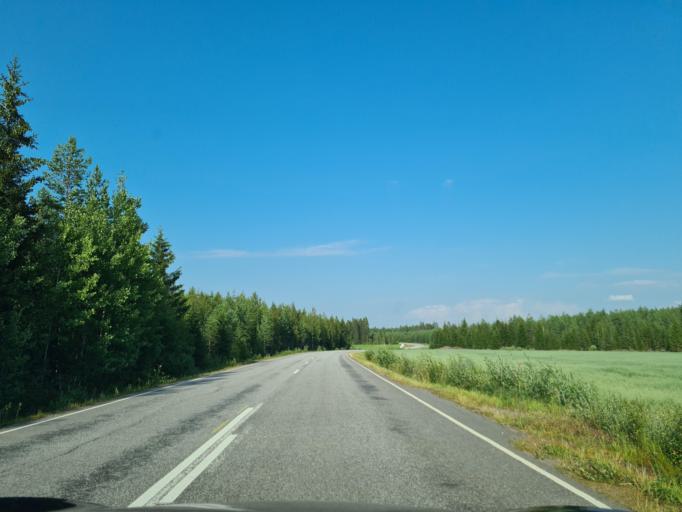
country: FI
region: Satakunta
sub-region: Pohjois-Satakunta
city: Karvia
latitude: 62.2924
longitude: 22.6133
